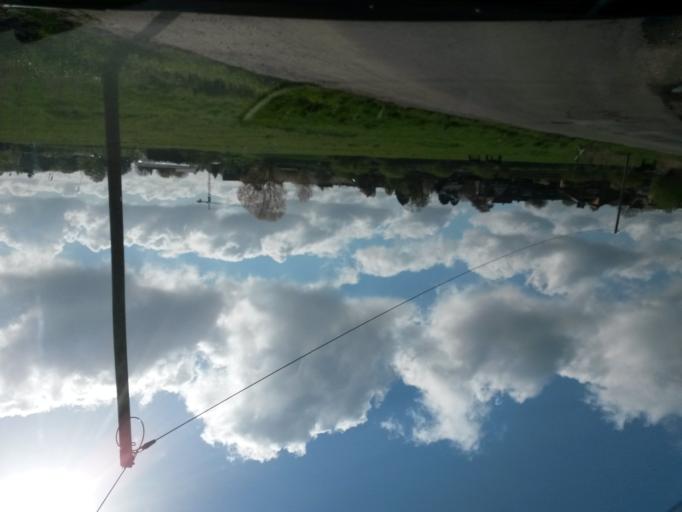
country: DE
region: Schleswig-Holstein
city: Wedel
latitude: 53.5866
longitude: 9.6837
